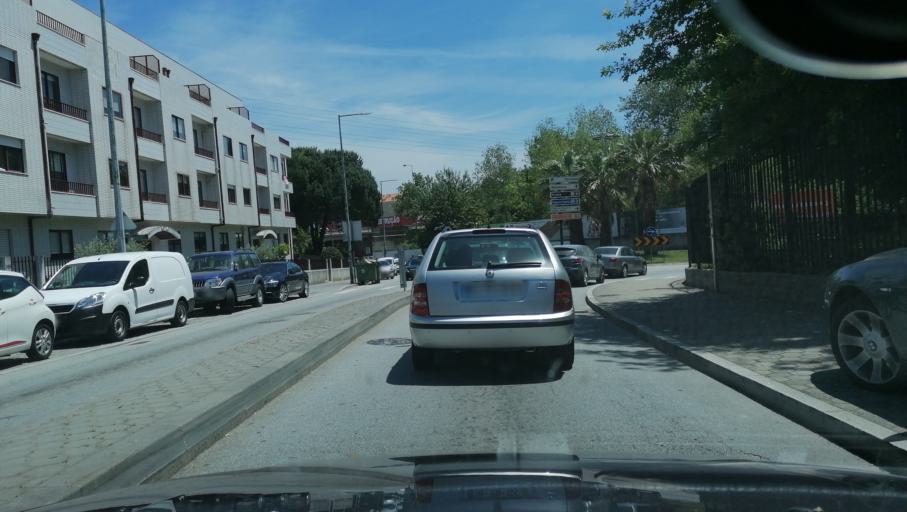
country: PT
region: Porto
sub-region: Vila Nova de Gaia
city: Canidelo
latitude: 41.1263
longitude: -8.6372
